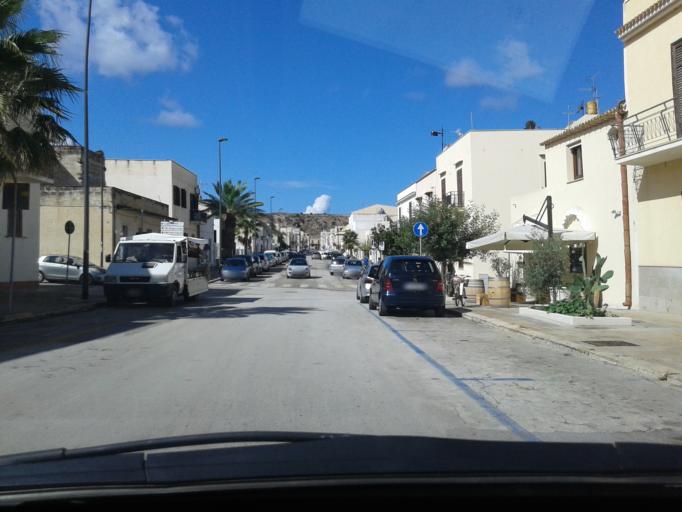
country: IT
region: Sicily
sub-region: Trapani
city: San Vito Lo Capo
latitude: 38.1736
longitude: 12.7384
